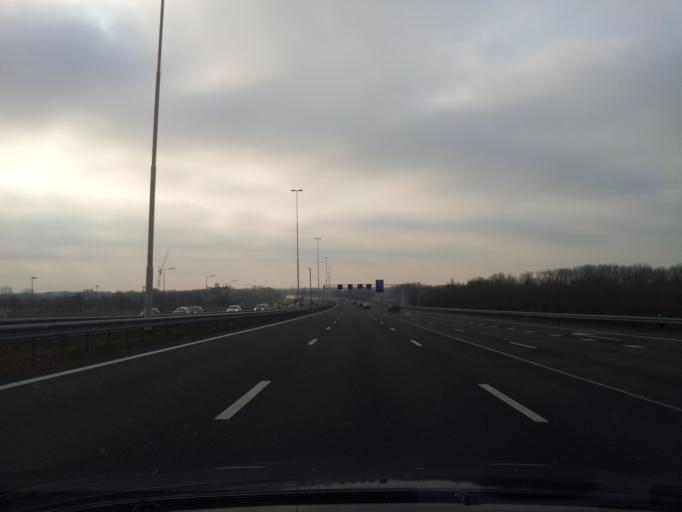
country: NL
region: Utrecht
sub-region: Gemeente Vianen
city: Vianen
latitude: 51.9951
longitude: 5.0791
